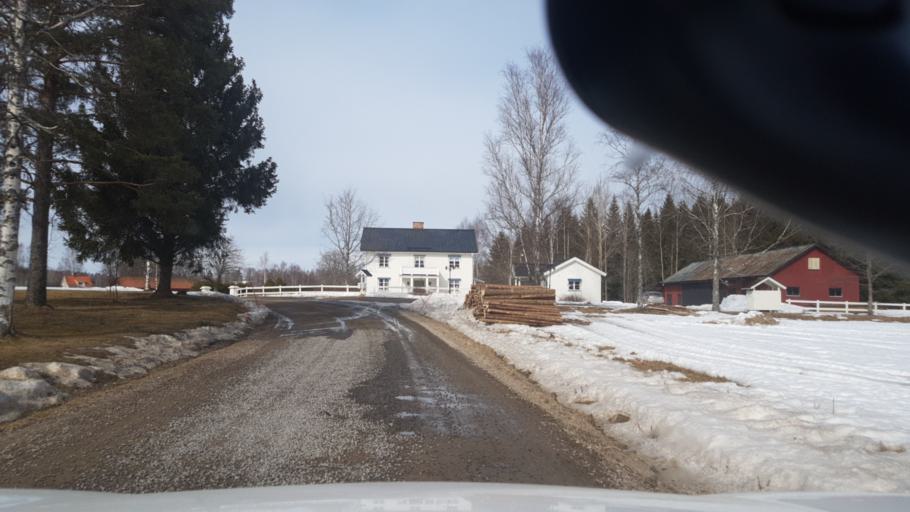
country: SE
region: Vaermland
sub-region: Eda Kommun
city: Charlottenberg
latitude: 59.8420
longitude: 12.3585
